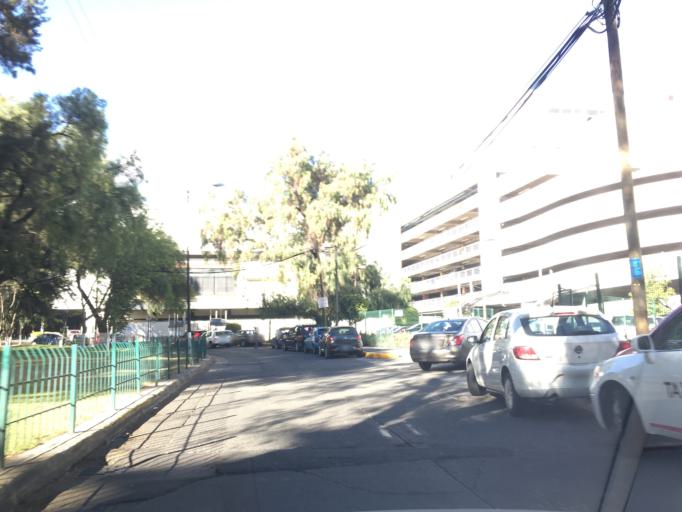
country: MX
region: Mexico
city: Colonia Lindavista
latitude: 19.4845
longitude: -99.1305
